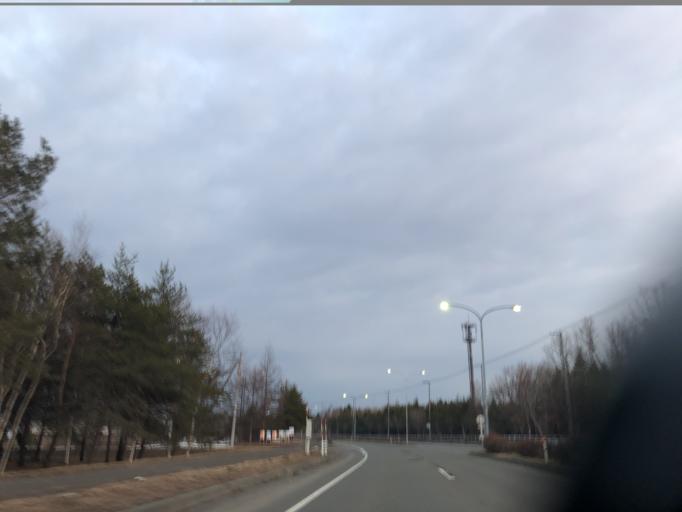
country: JP
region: Hokkaido
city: Chitose
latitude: 42.8228
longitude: 141.6716
